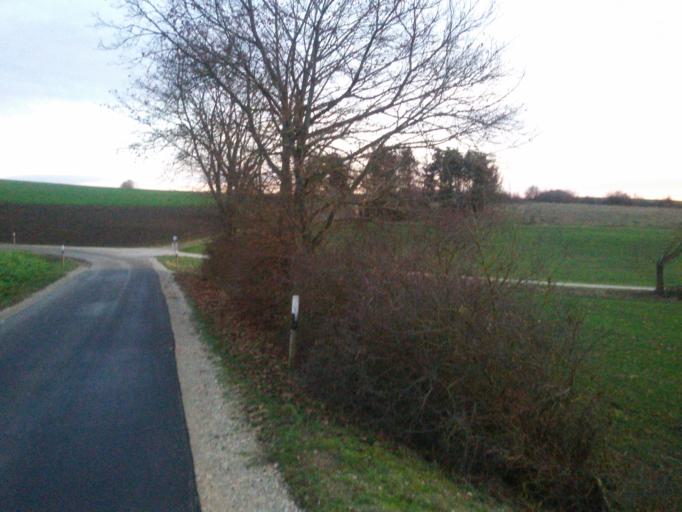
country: DE
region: Bavaria
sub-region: Swabia
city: Huisheim
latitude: 48.8102
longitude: 10.7263
